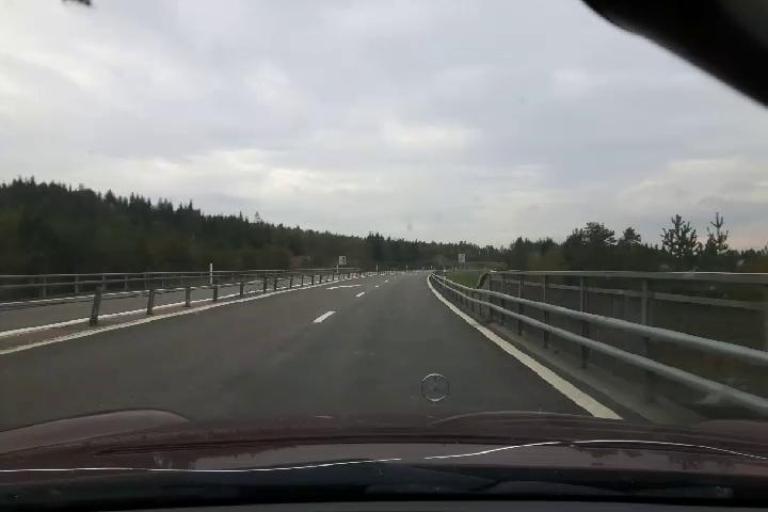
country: SE
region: Vaesternorrland
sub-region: Haernoesands Kommun
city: Haernoesand
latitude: 62.7202
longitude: 17.9172
